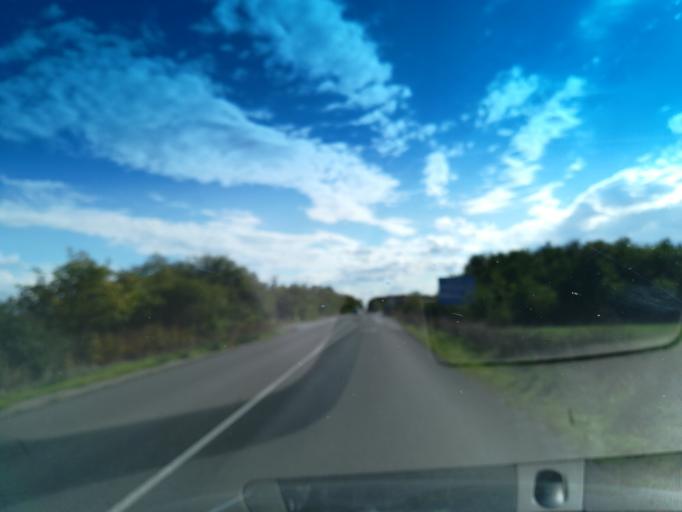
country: BG
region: Stara Zagora
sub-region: Obshtina Stara Zagora
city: Stara Zagora
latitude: 42.3586
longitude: 25.6565
